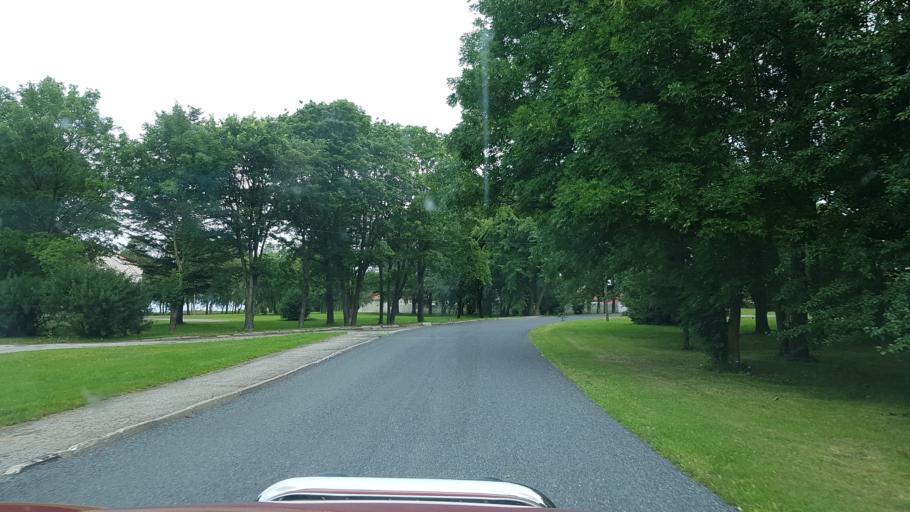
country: EE
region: Ida-Virumaa
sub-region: Aseri vald
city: Aseri
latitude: 59.4520
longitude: 26.8685
